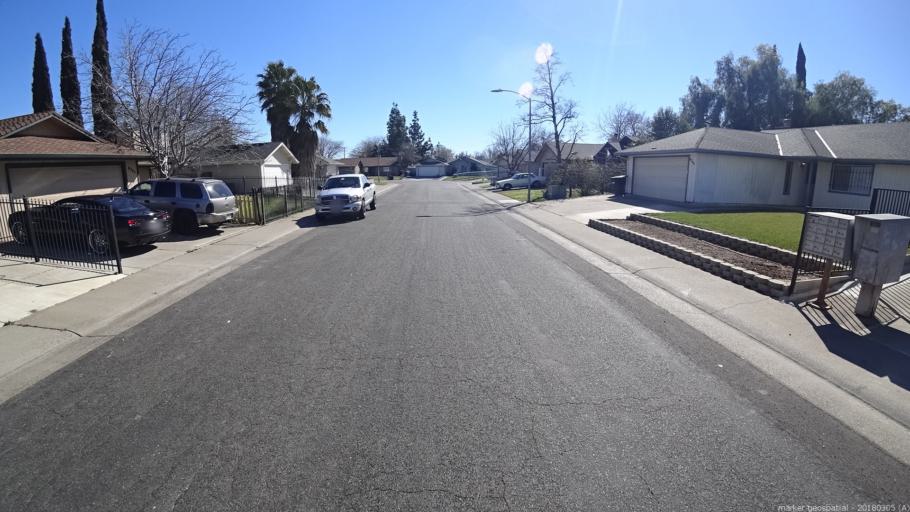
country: US
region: California
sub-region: Sacramento County
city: Florin
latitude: 38.4933
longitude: -121.4017
